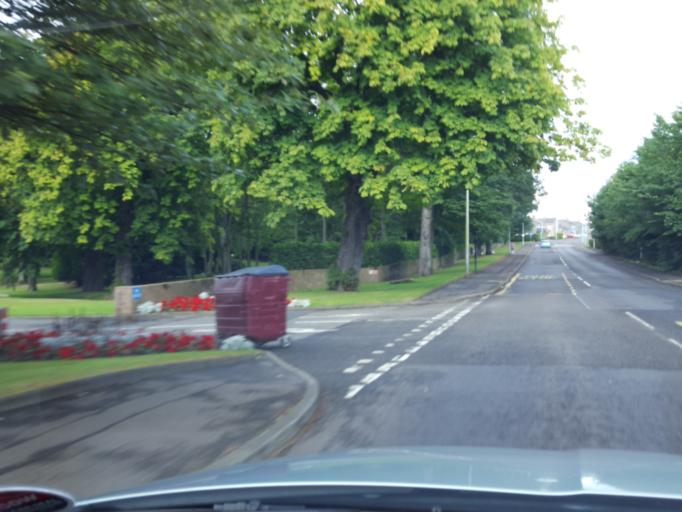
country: GB
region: Scotland
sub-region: Fife
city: Inverkeithing
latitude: 56.0546
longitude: -3.4141
